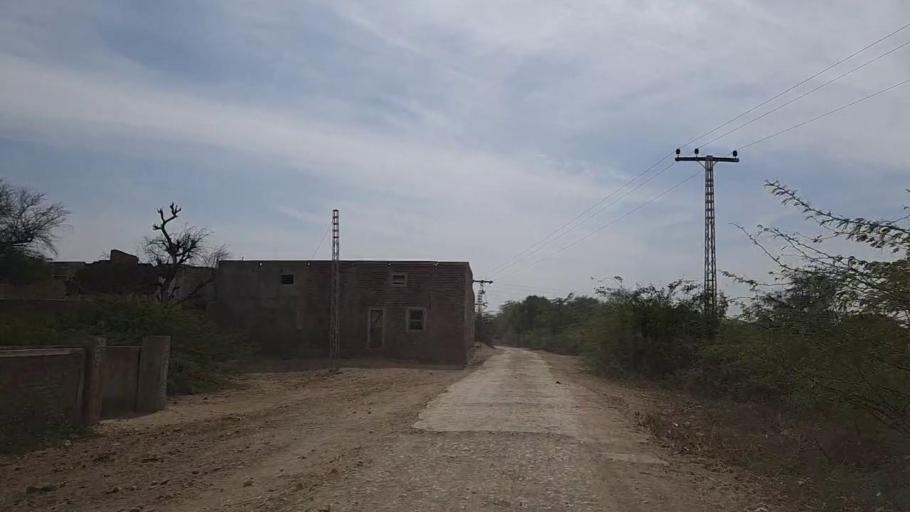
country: PK
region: Sindh
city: Samaro
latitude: 25.2651
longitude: 69.4536
